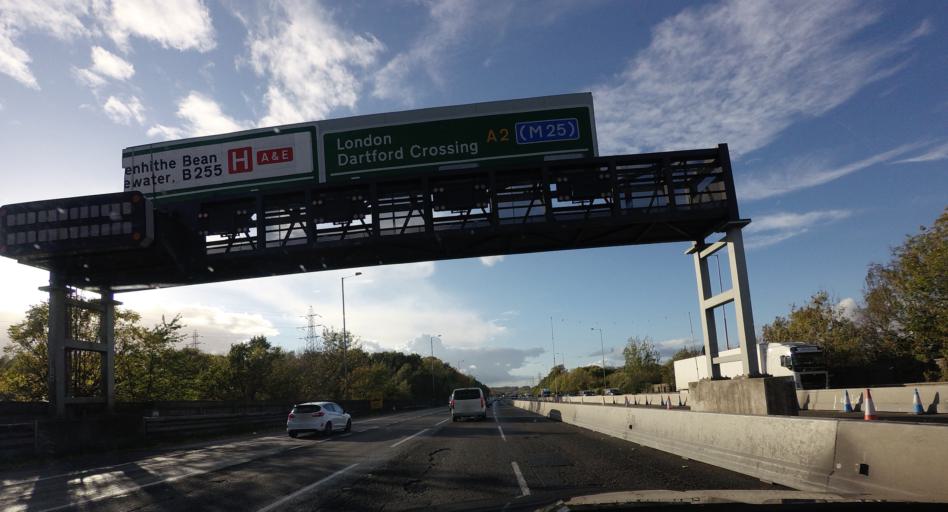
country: GB
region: England
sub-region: Kent
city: Greenhithe
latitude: 51.4305
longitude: 0.2926
